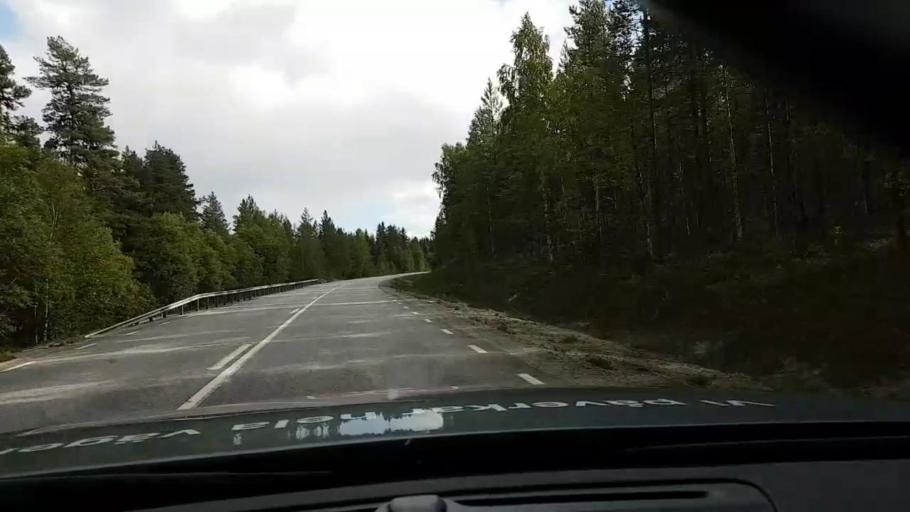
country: SE
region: Vaesternorrland
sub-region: OErnskoeldsviks Kommun
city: Bredbyn
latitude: 63.6345
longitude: 17.9070
